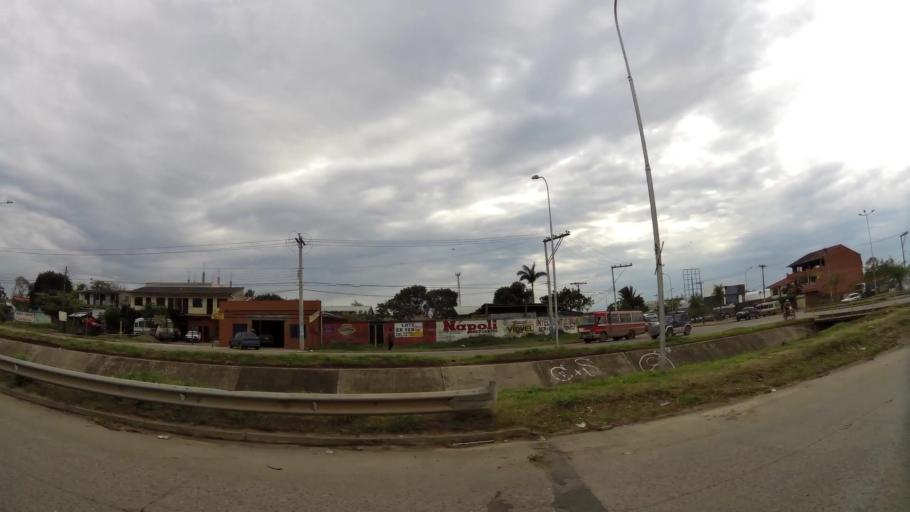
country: BO
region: Santa Cruz
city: Santa Cruz de la Sierra
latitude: -17.7372
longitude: -63.1547
